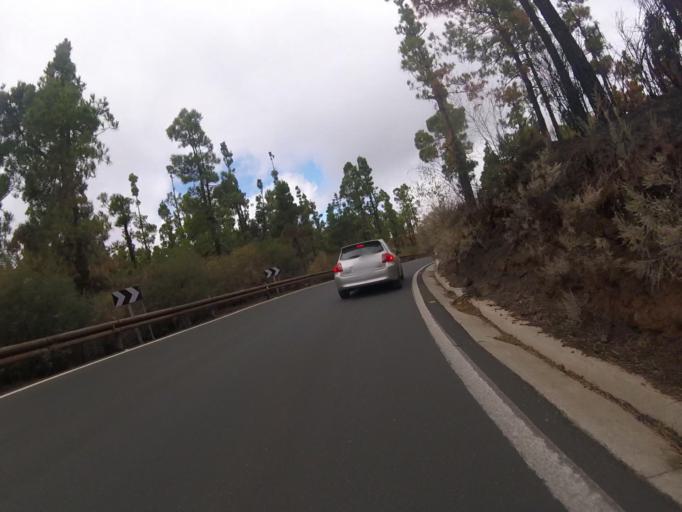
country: ES
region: Canary Islands
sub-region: Provincia de Las Palmas
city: San Bartolome
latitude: 27.9686
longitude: -15.5677
